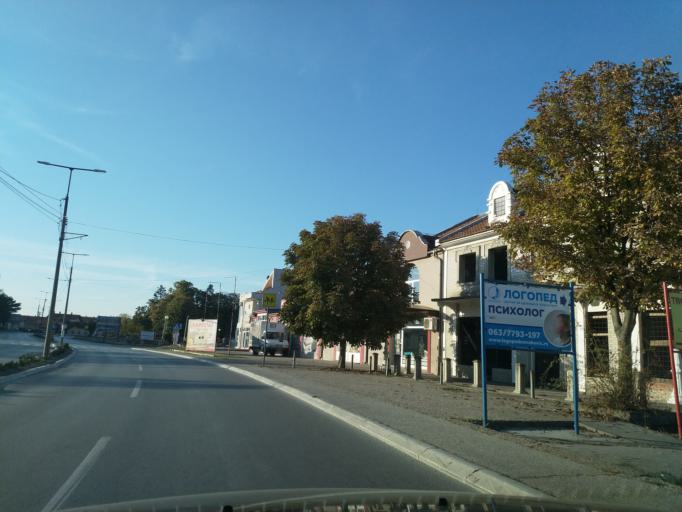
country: RS
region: Central Serbia
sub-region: Pomoravski Okrug
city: Svilajnac
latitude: 44.2294
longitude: 21.1955
